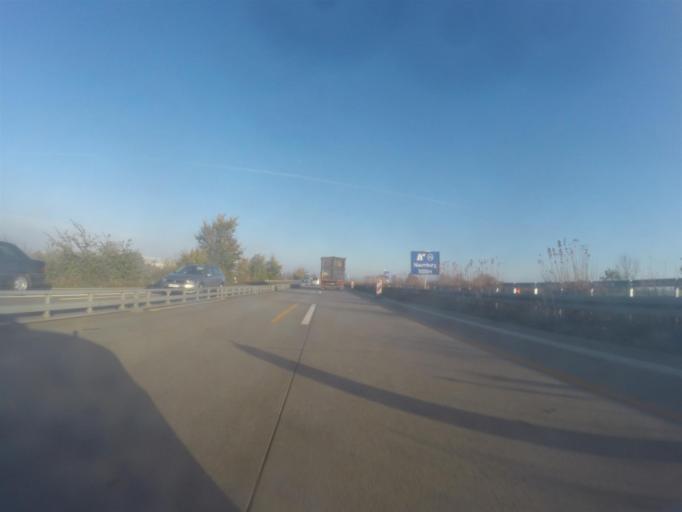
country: DE
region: Saxony-Anhalt
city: Osterfeld
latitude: 51.0800
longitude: 11.9554
